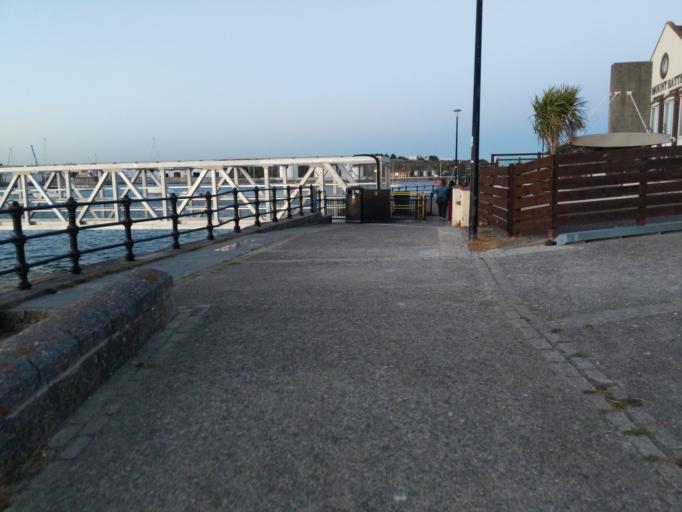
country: GB
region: England
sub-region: Plymouth
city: Plymouth
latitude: 50.3606
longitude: -4.1305
